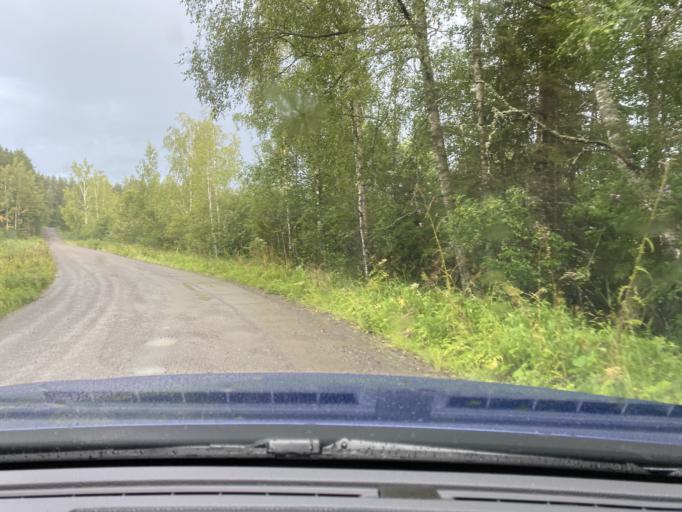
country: FI
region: Pirkanmaa
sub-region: Lounais-Pirkanmaa
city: Punkalaidun
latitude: 61.0612
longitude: 23.2445
